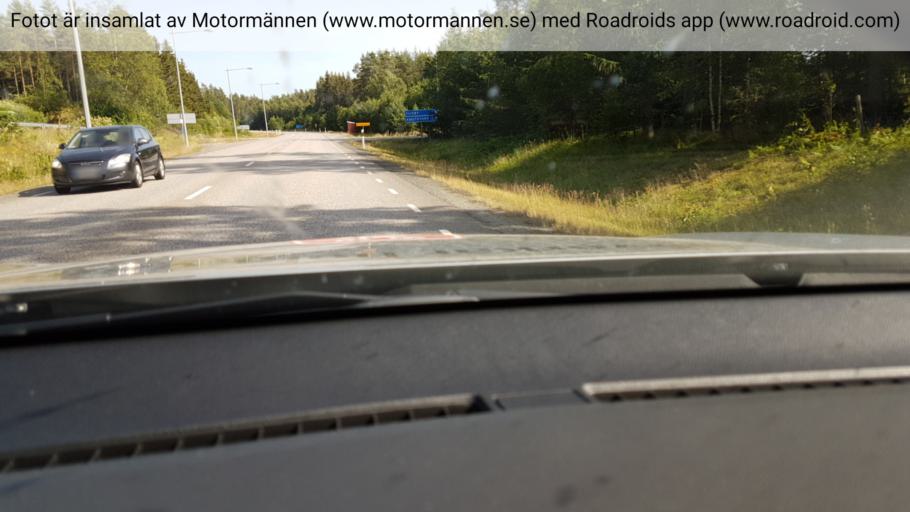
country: SE
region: Joenkoeping
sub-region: Eksjo Kommun
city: Eksjoe
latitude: 57.7643
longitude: 14.9074
